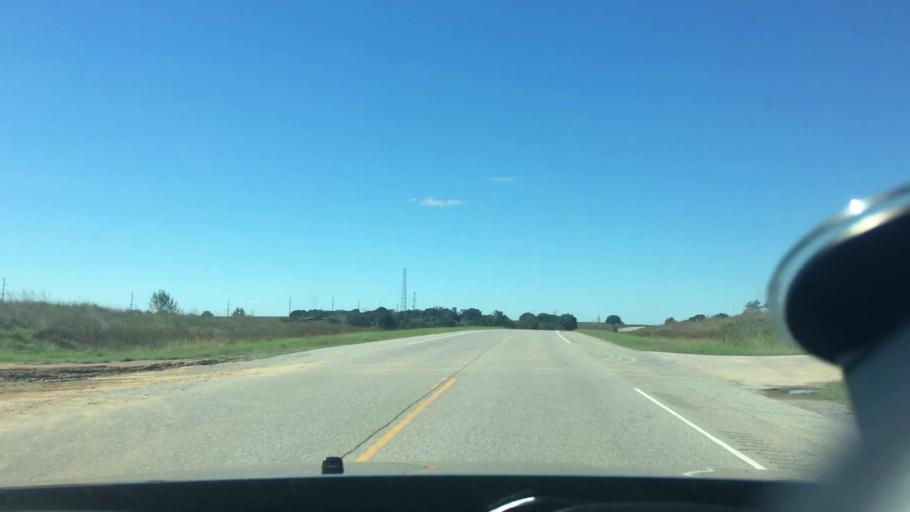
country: US
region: Oklahoma
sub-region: Coal County
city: Coalgate
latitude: 34.6140
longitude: -96.4416
